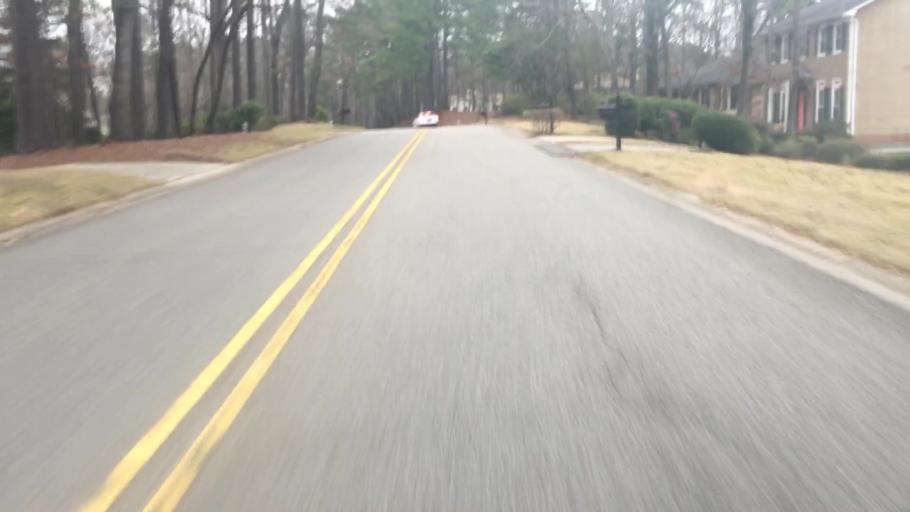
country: US
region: Alabama
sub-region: Shelby County
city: Indian Springs Village
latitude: 33.3496
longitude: -86.8090
